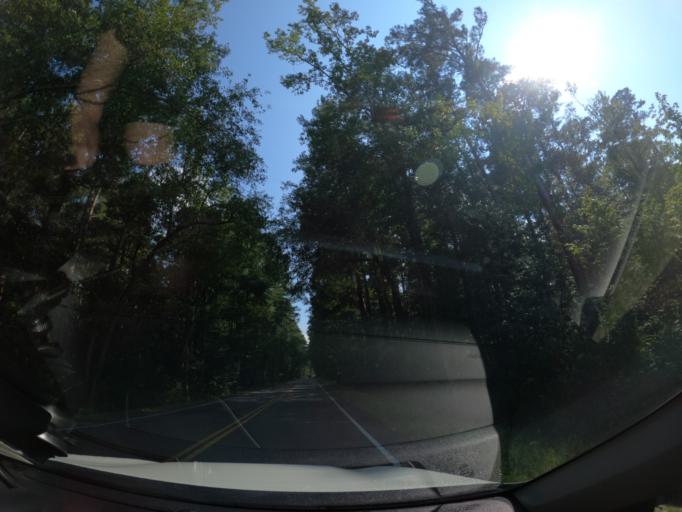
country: US
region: South Carolina
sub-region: Barnwell County
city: Williston
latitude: 33.5598
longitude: -81.4818
